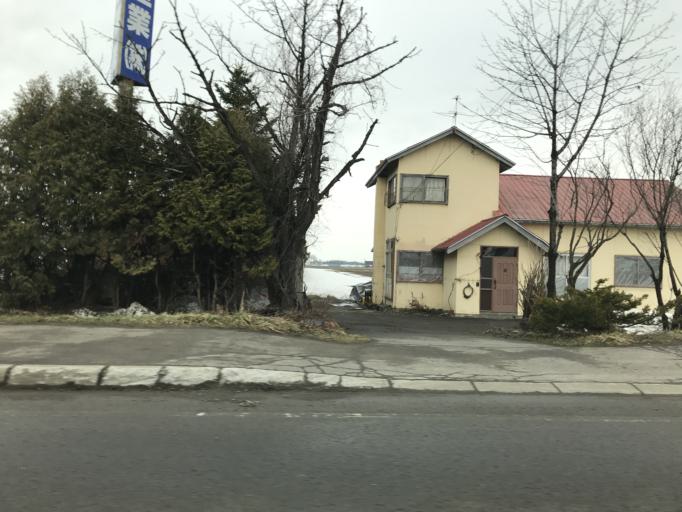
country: JP
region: Hokkaido
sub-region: Asahikawa-shi
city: Asahikawa
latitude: 43.8276
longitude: 142.4199
